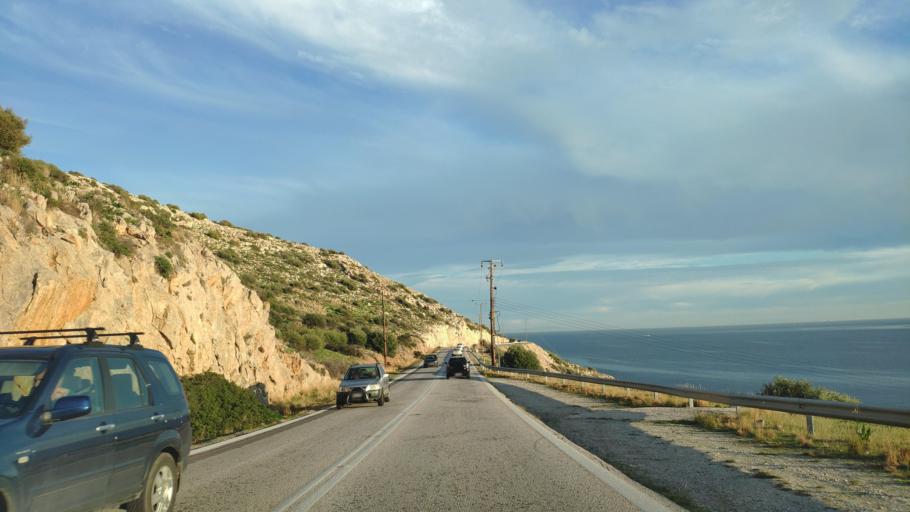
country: GR
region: Attica
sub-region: Nomarchia Anatolikis Attikis
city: Palaia Fokaia
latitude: 37.6712
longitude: 23.9478
